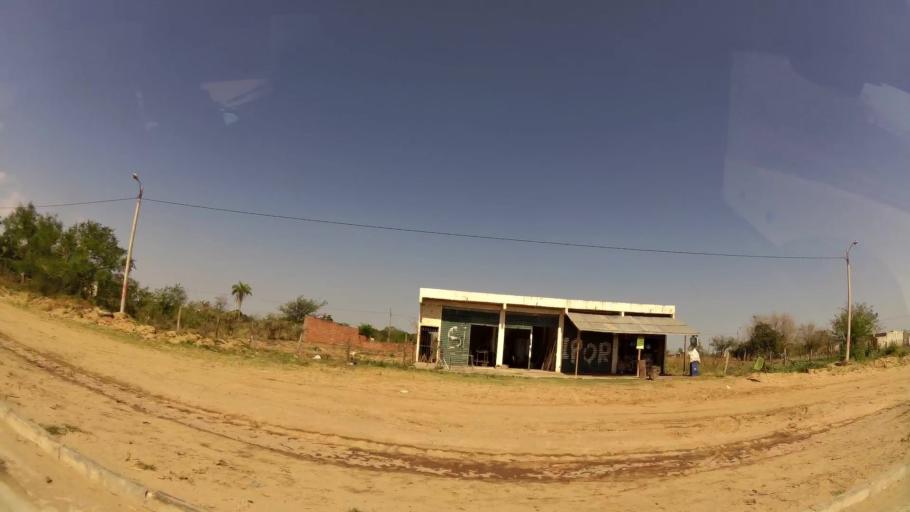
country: BO
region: Santa Cruz
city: Cotoca
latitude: -17.7205
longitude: -63.0752
